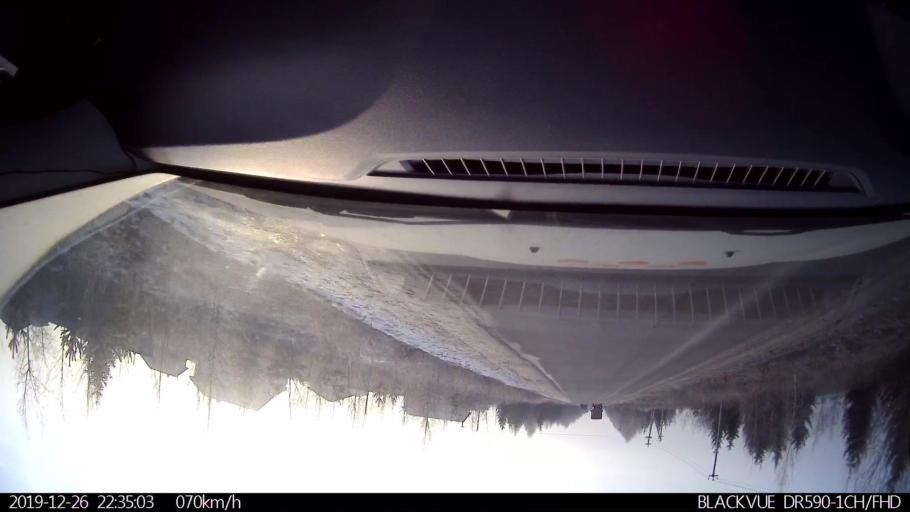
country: RU
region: Nizjnij Novgorod
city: Burevestnik
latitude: 56.1505
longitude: 43.7160
